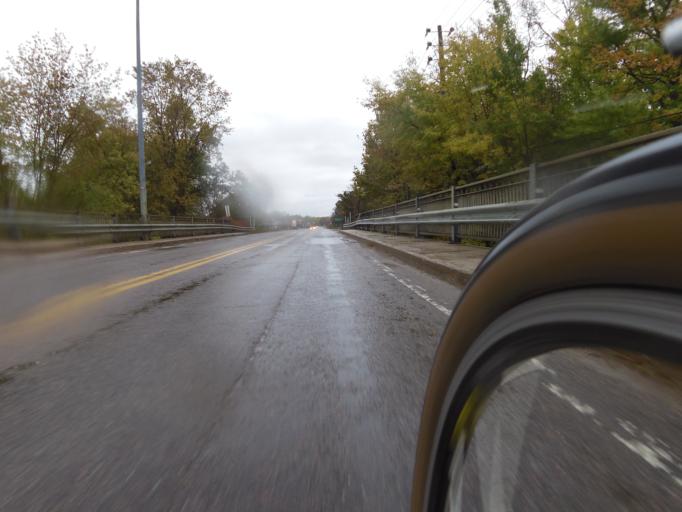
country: CA
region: Quebec
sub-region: Outaouais
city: Fort-Coulonge
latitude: 45.8508
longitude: -76.7295
